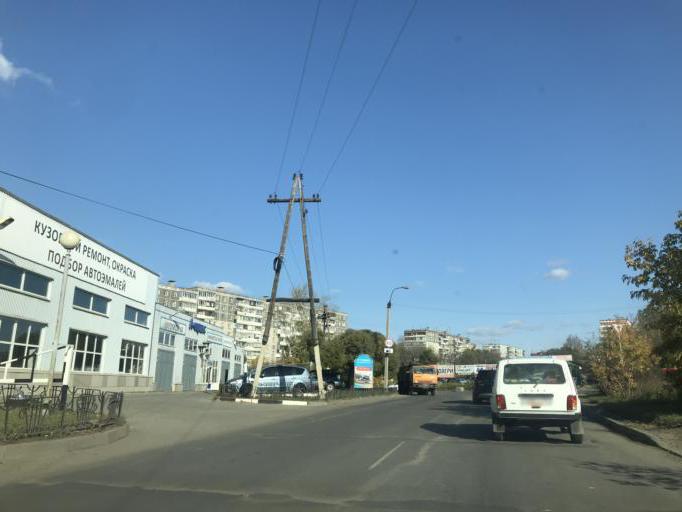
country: RU
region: Chelyabinsk
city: Dolgoderevenskoye
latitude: 55.2573
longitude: 61.3622
